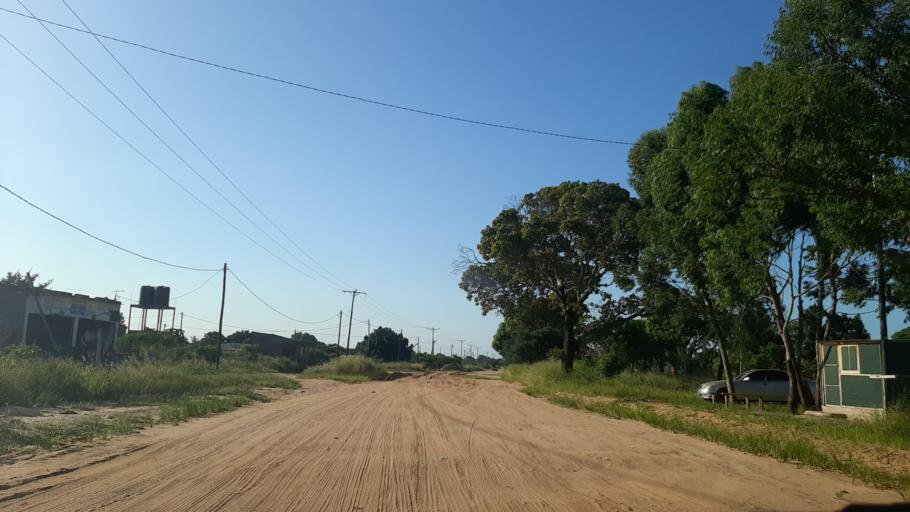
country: MZ
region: Maputo City
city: Maputo
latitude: -25.7701
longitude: 32.5486
